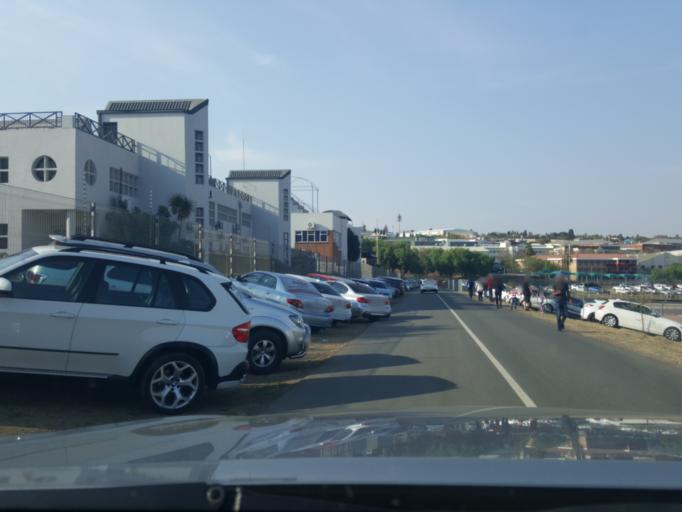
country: ZA
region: Gauteng
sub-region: City of Johannesburg Metropolitan Municipality
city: Midrand
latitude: -25.9942
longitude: 28.0706
